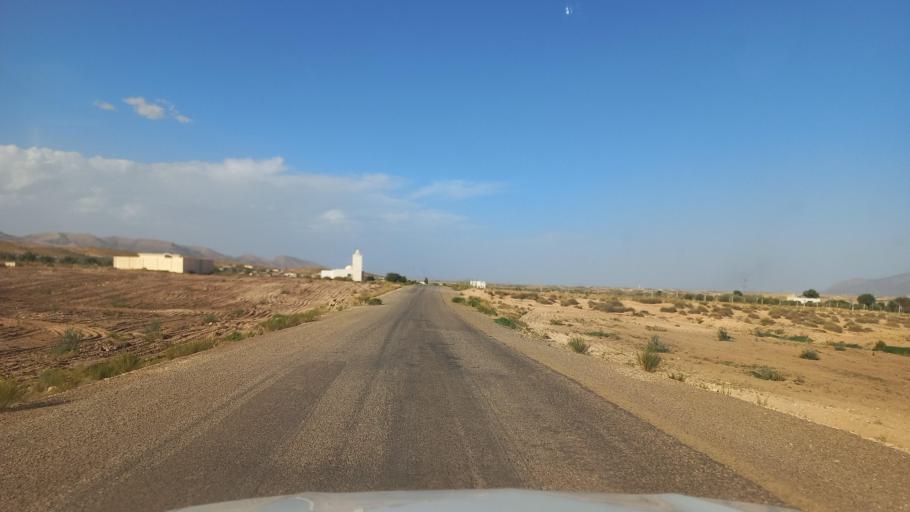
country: TN
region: Al Qasrayn
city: Sbiba
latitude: 35.3673
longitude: 9.0082
